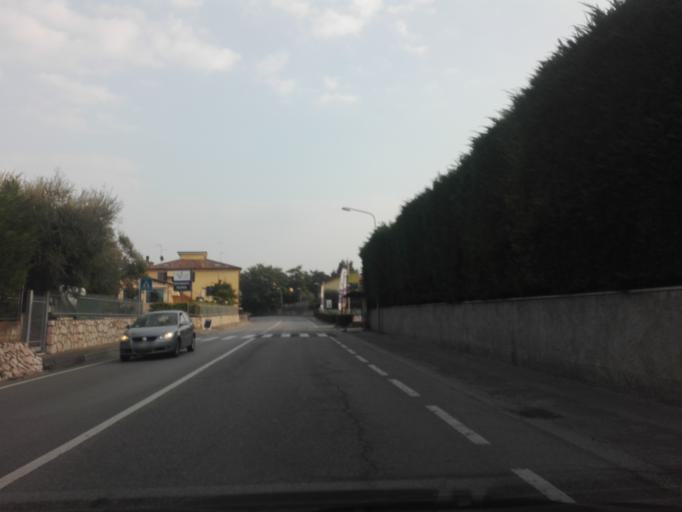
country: IT
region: Veneto
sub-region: Provincia di Verona
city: Lazise
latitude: 45.5006
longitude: 10.7473
